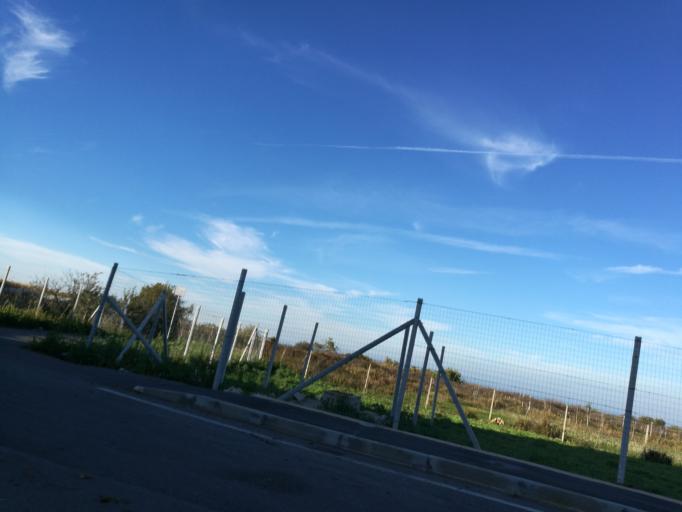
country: IT
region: Apulia
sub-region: Provincia di Bari
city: Adelfia
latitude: 41.0076
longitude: 16.8698
